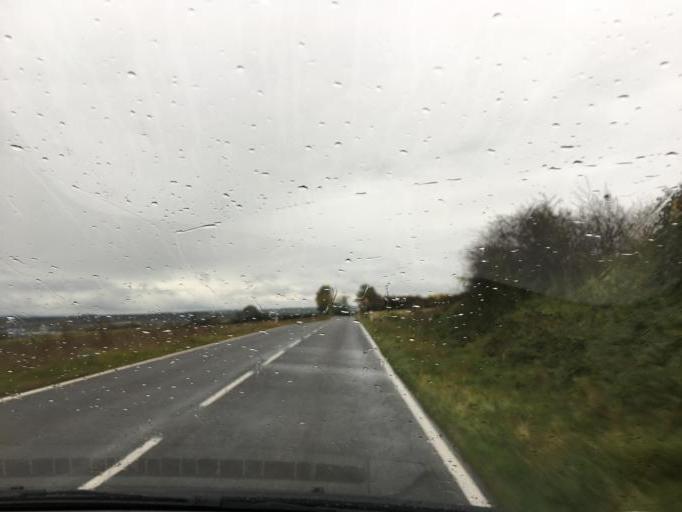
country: DE
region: North Rhine-Westphalia
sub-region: Regierungsbezirk Koln
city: Vettweiss
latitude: 50.7057
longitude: 6.5743
